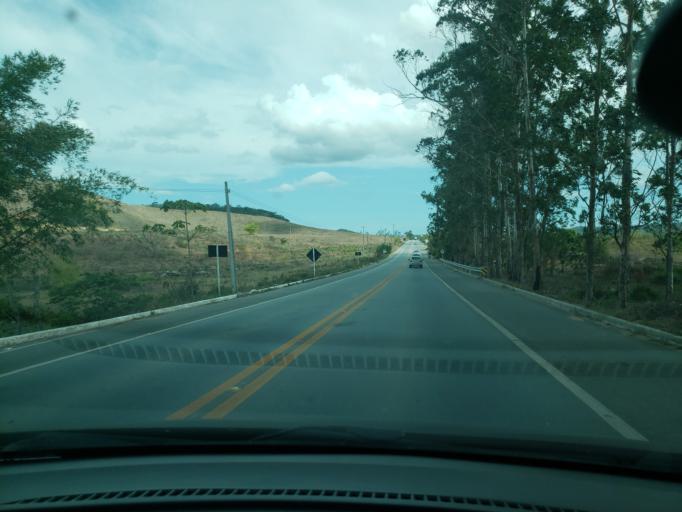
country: BR
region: Alagoas
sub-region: Murici
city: Murici
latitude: -9.3137
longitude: -35.9328
